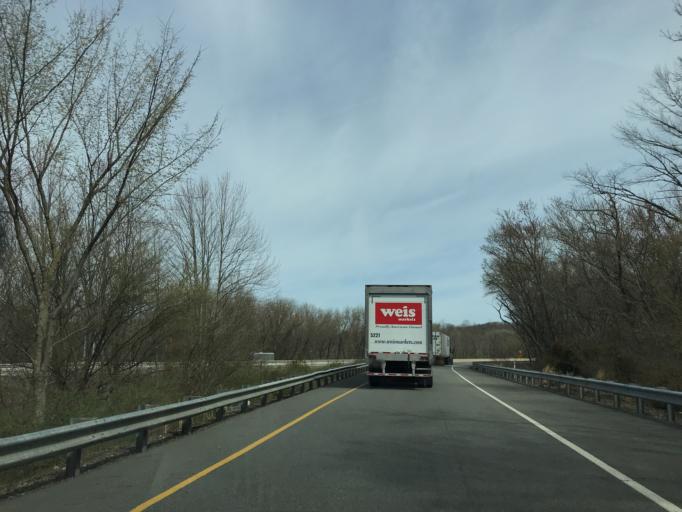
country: US
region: Pennsylvania
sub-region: Perry County
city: Duncannon
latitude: 40.4234
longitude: -77.0071
